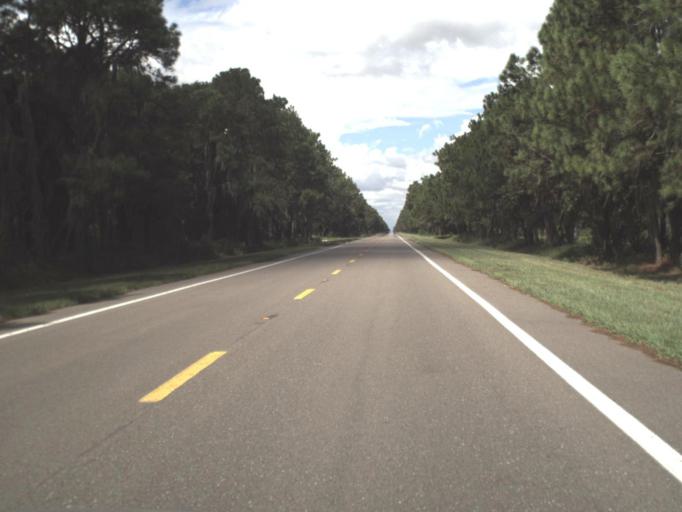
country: US
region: Florida
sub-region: Polk County
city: Mulberry
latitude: 27.7048
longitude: -82.0281
